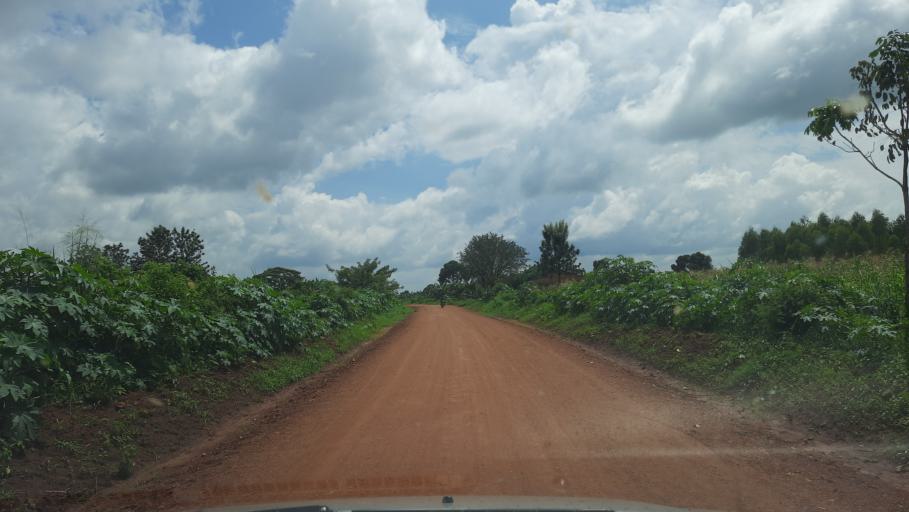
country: UG
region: Western Region
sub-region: Kiryandongo District
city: Kiryandongo
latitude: 1.8213
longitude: 31.9837
